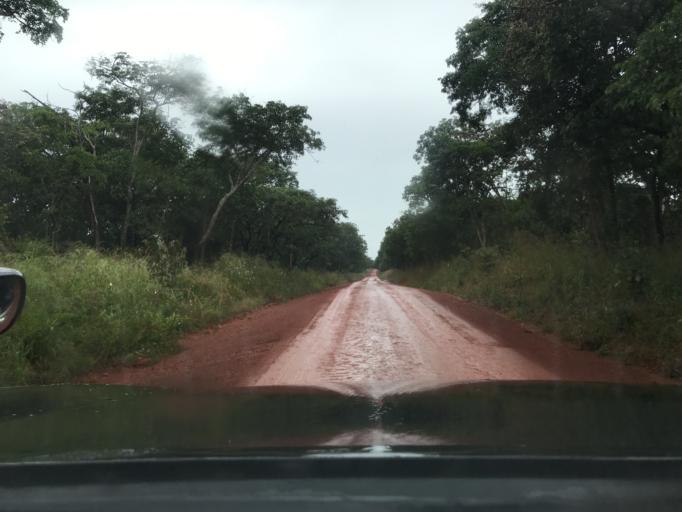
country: TZ
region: Kigoma
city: Uvinza
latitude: -5.2857
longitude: 30.3690
